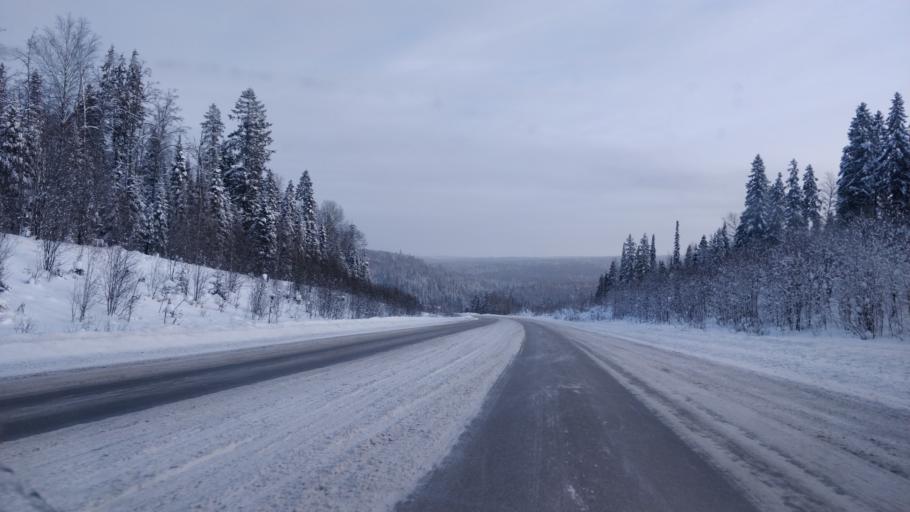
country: RU
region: Perm
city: Polazna
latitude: 58.2890
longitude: 56.4989
